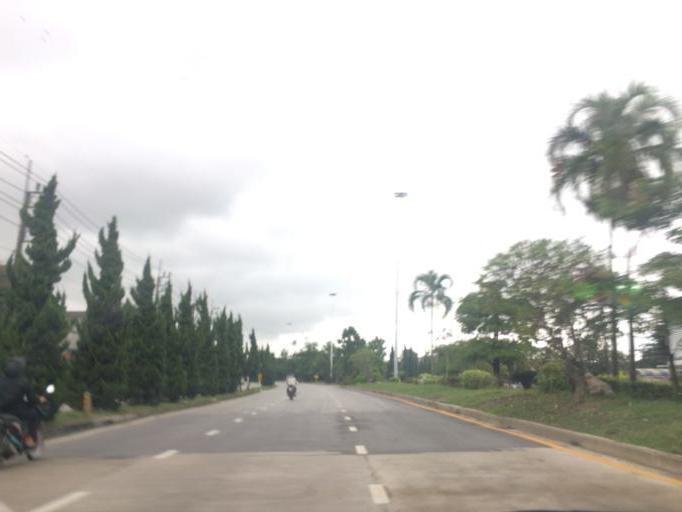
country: TH
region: Chiang Rai
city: Chiang Rai
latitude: 19.9033
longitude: 99.8405
